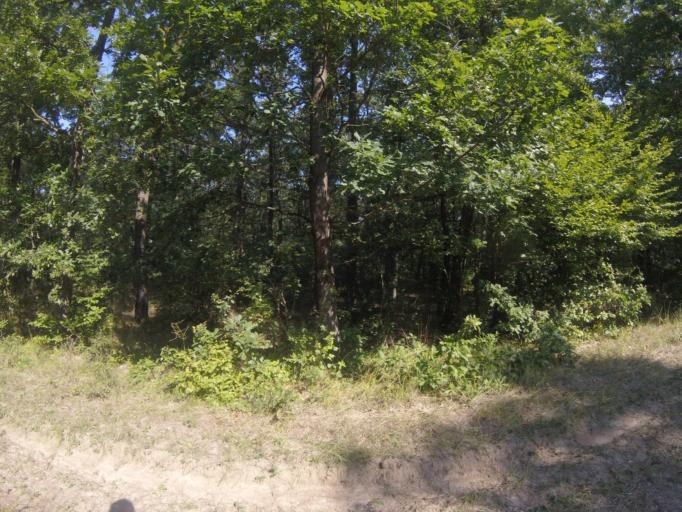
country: HU
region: Nograd
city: Bujak
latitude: 47.8966
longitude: 19.5131
